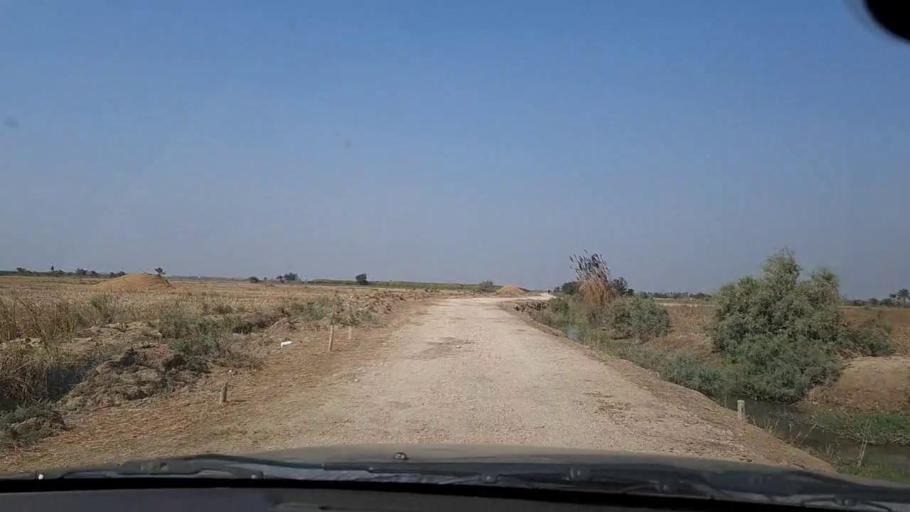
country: PK
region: Sindh
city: Mirpur Sakro
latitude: 24.3622
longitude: 67.6831
